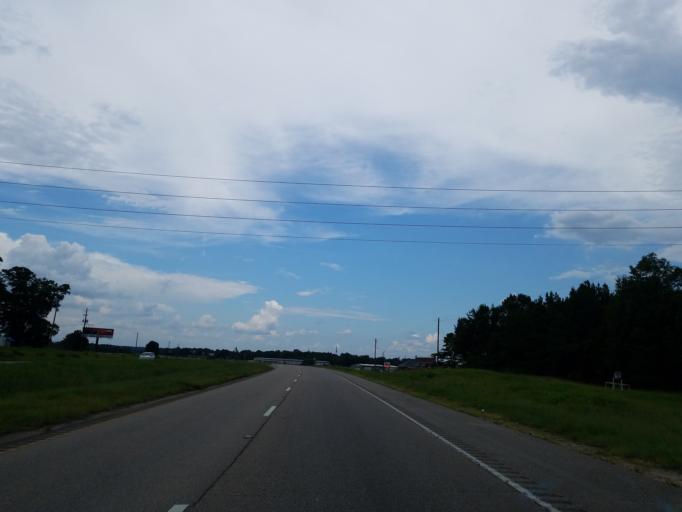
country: US
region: Mississippi
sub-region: Forrest County
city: Glendale
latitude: 31.3612
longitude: -89.2984
